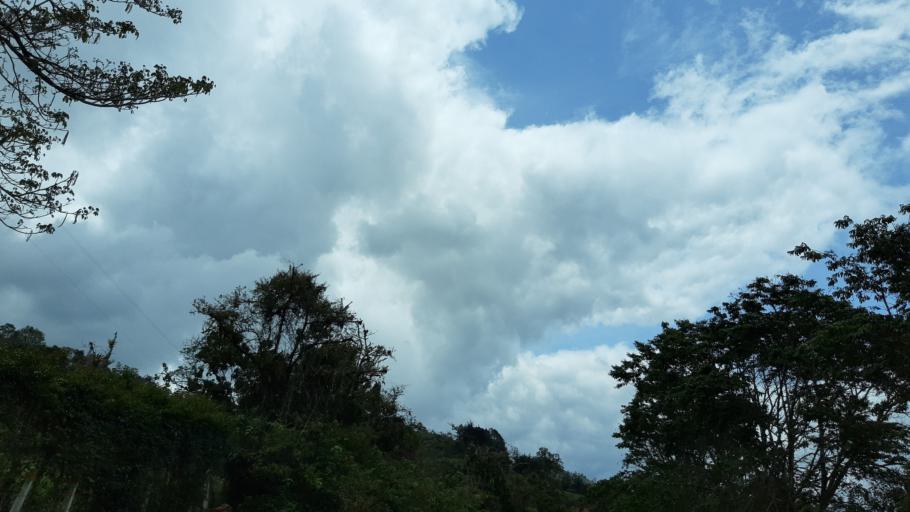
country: CO
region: Boyaca
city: Garagoa
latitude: 5.0679
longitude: -73.3622
